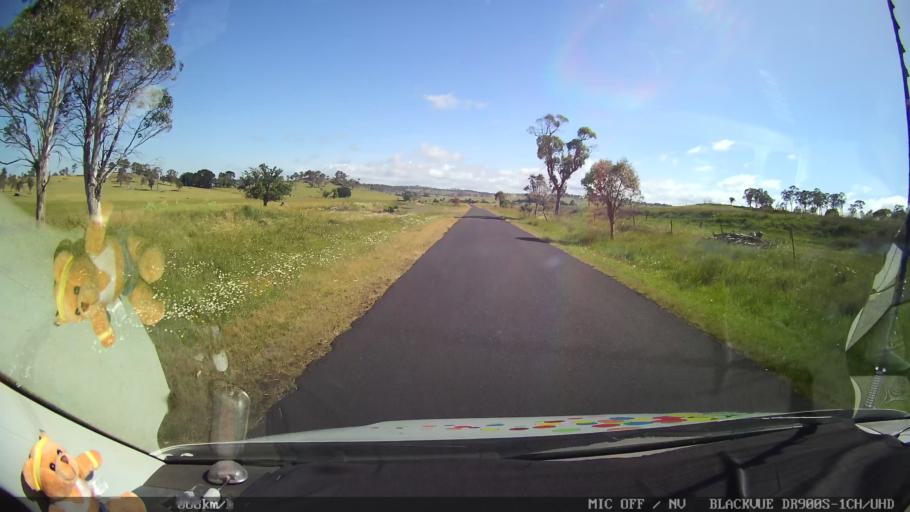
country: AU
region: New South Wales
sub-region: Guyra
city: Guyra
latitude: -30.1537
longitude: 151.6812
